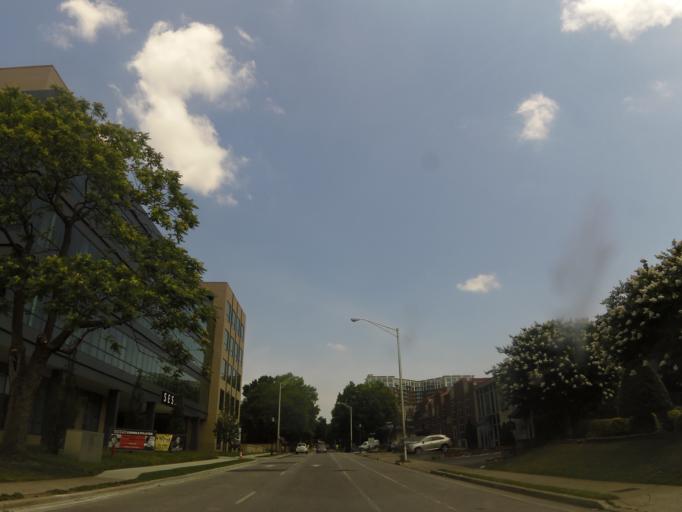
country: US
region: Tennessee
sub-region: Davidson County
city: Nashville
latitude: 36.1485
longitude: -86.7922
